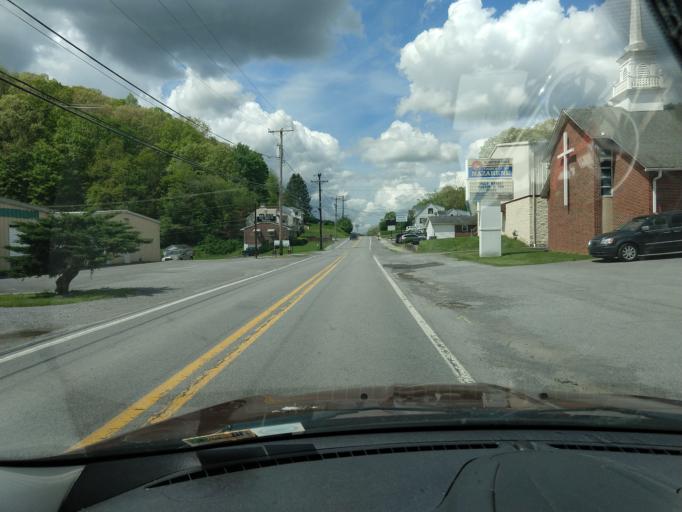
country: US
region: West Virginia
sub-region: Mercer County
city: Bluefield
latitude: 37.2534
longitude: -81.2362
